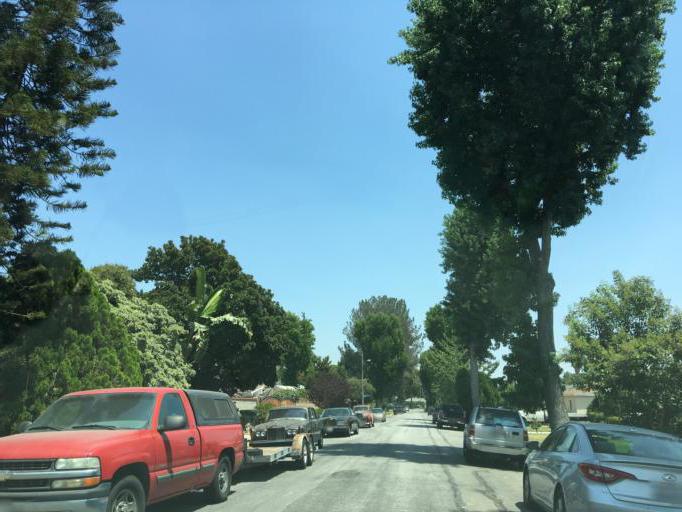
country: US
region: California
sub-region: Los Angeles County
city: Mayflower Village
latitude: 34.1131
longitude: -118.0122
